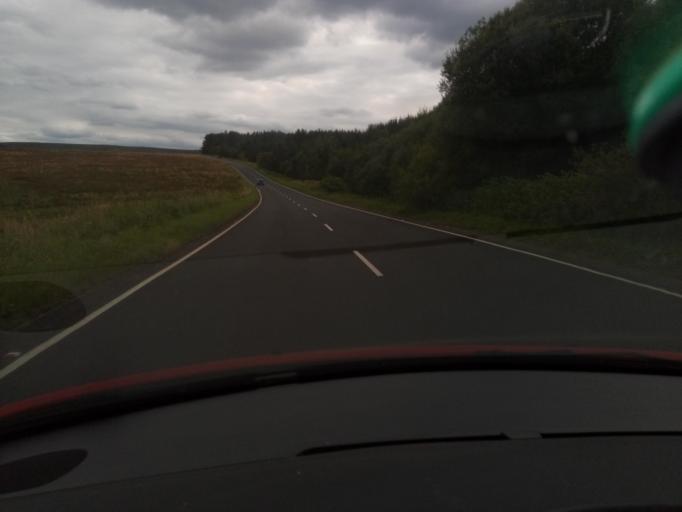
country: GB
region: Scotland
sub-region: The Scottish Borders
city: Jedburgh
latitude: 55.3767
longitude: -2.4942
